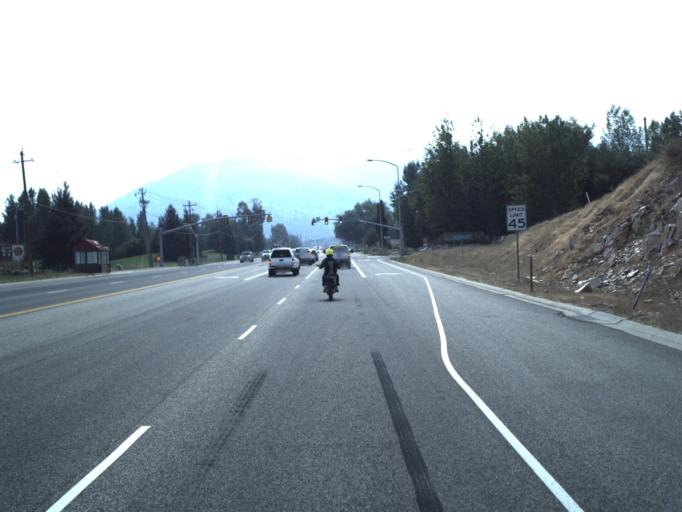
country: US
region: Utah
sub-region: Summit County
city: Snyderville
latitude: 40.6979
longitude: -111.5444
